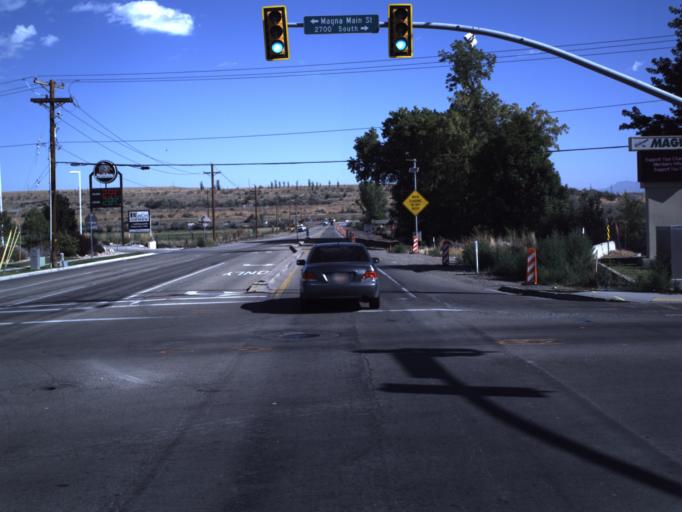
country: US
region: Utah
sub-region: Salt Lake County
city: Magna
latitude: 40.7110
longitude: -112.0917
